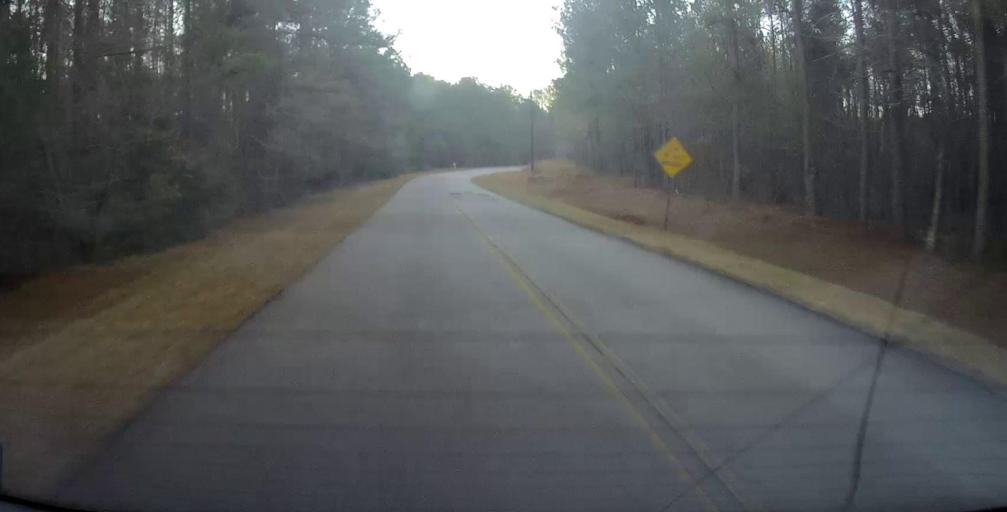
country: US
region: Georgia
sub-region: Harris County
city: Hamilton
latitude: 32.6151
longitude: -84.8523
